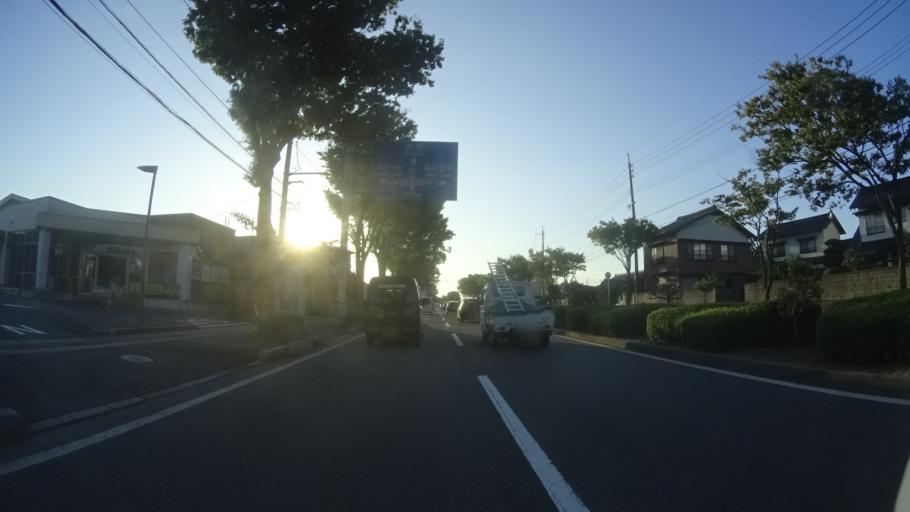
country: JP
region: Tottori
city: Yonago
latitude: 35.4507
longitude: 133.3604
